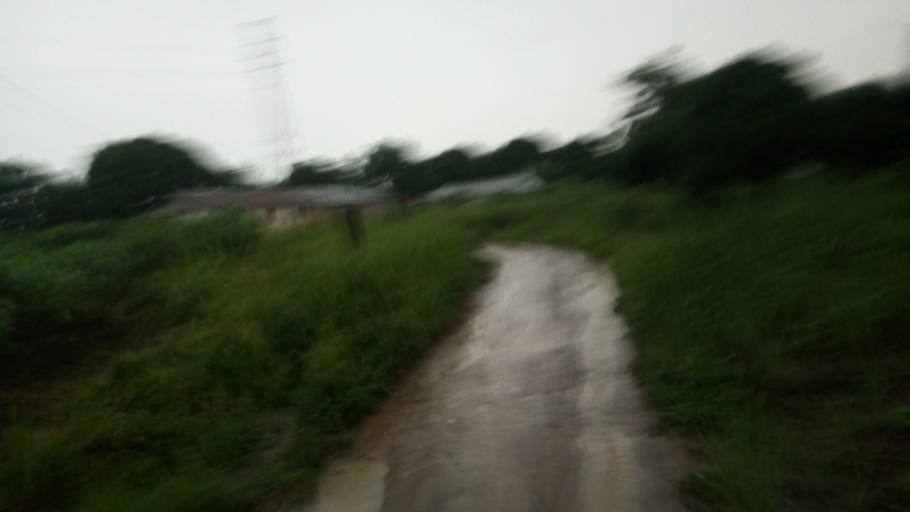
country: SL
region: Northern Province
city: Lunsar
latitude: 8.6959
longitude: -12.5329
